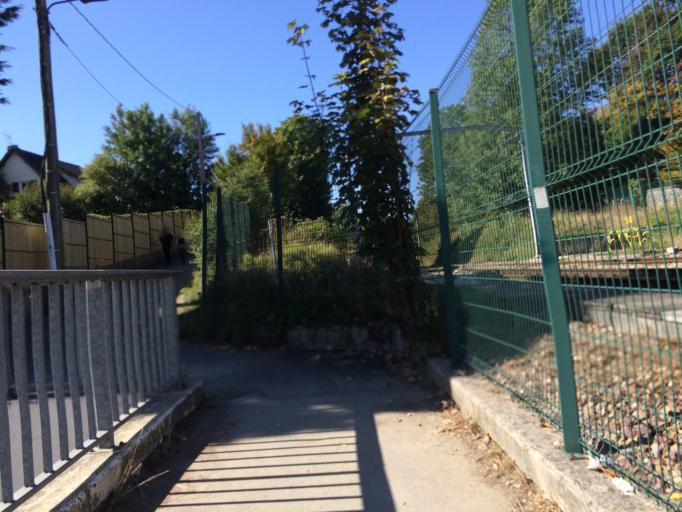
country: FR
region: Ile-de-France
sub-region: Departement de l'Essonne
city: Bures-sur-Yvette
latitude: 48.6952
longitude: 2.1625
